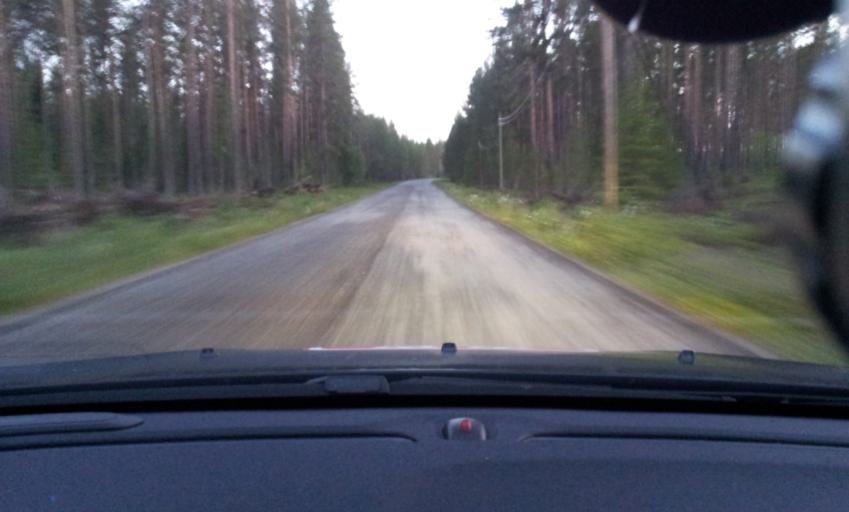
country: SE
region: Vaesternorrland
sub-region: Ange Kommun
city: Fransta
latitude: 62.7811
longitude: 16.0519
